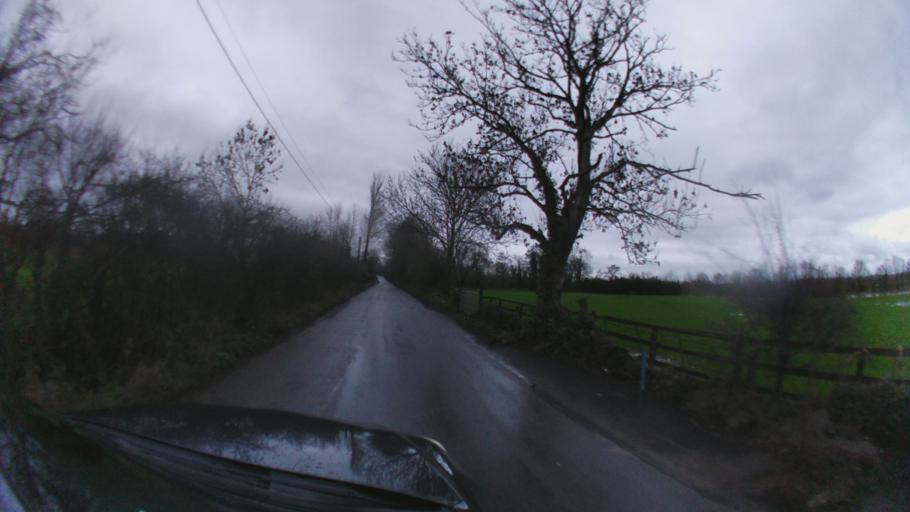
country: IE
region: Leinster
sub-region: County Carlow
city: Bagenalstown
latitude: 52.6530
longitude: -6.9895
